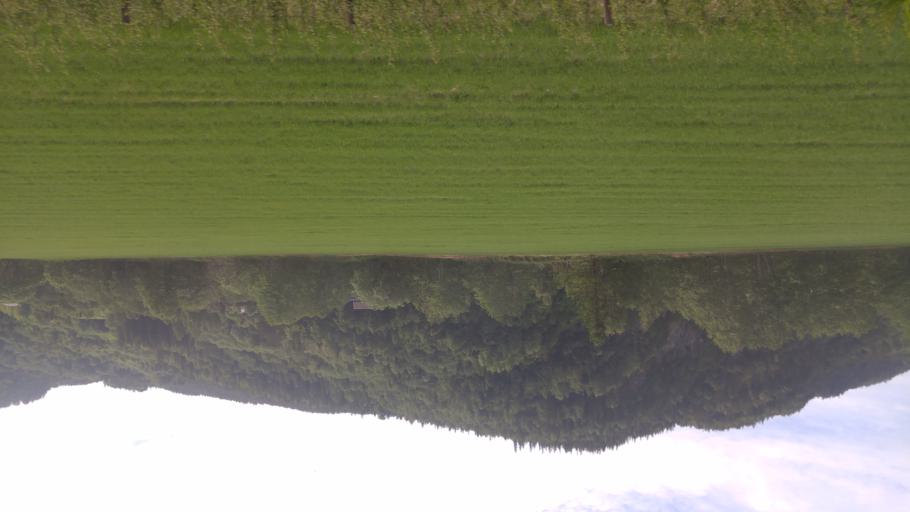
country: NO
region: Sor-Trondelag
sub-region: Midtre Gauldal
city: Storen
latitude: 63.0936
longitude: 10.2361
